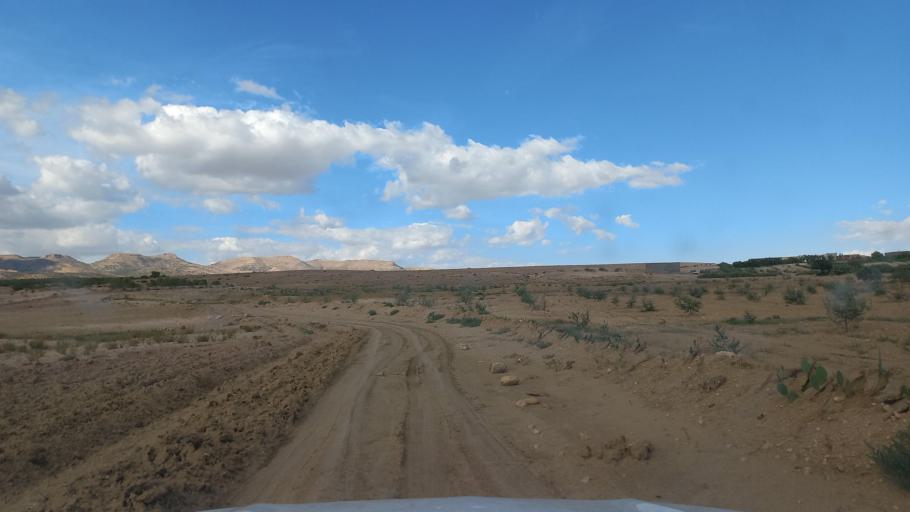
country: TN
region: Al Qasrayn
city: Sbiba
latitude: 35.4008
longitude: 9.0112
